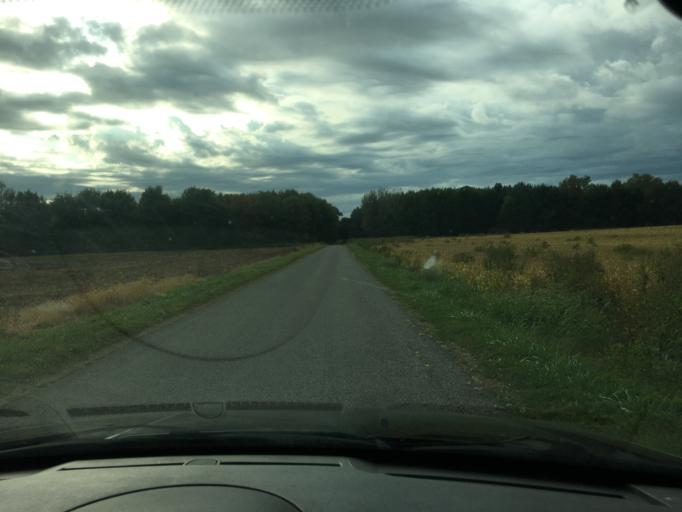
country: US
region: Ohio
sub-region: Logan County
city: West Liberty
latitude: 40.2571
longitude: -83.7377
